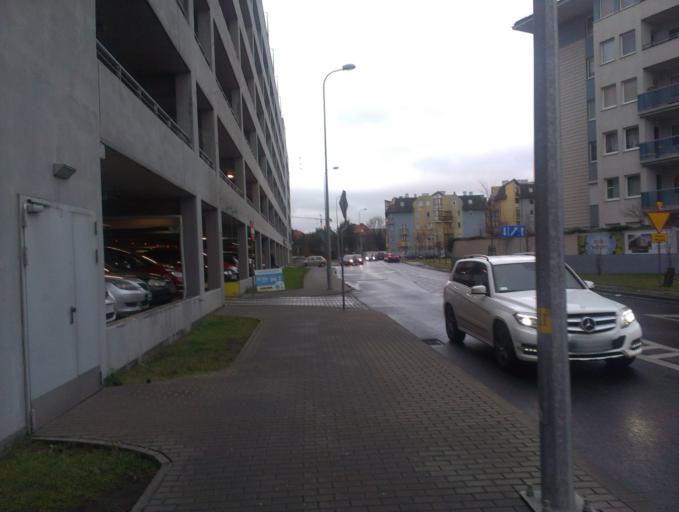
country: PL
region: Greater Poland Voivodeship
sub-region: Poznan
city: Poznan
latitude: 52.4018
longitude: 16.9577
